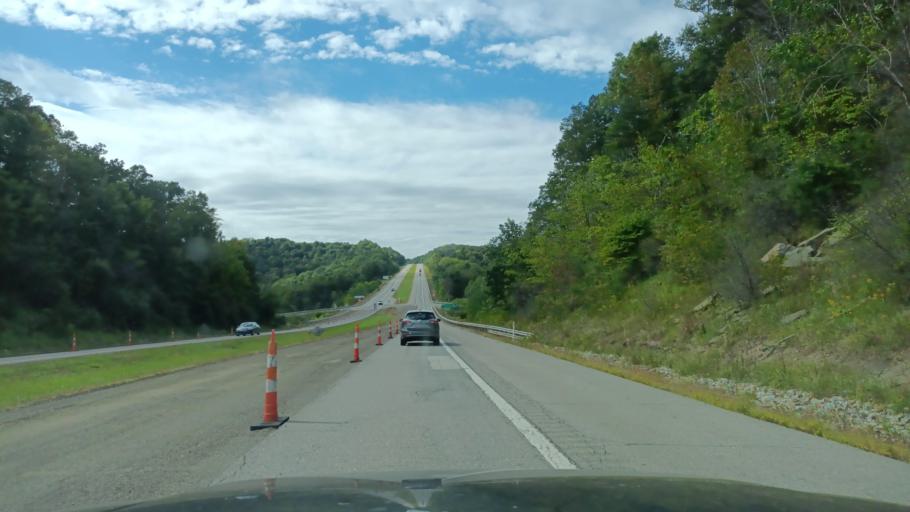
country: US
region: West Virginia
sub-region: Ritchie County
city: Harrisville
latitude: 39.2612
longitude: -81.1378
